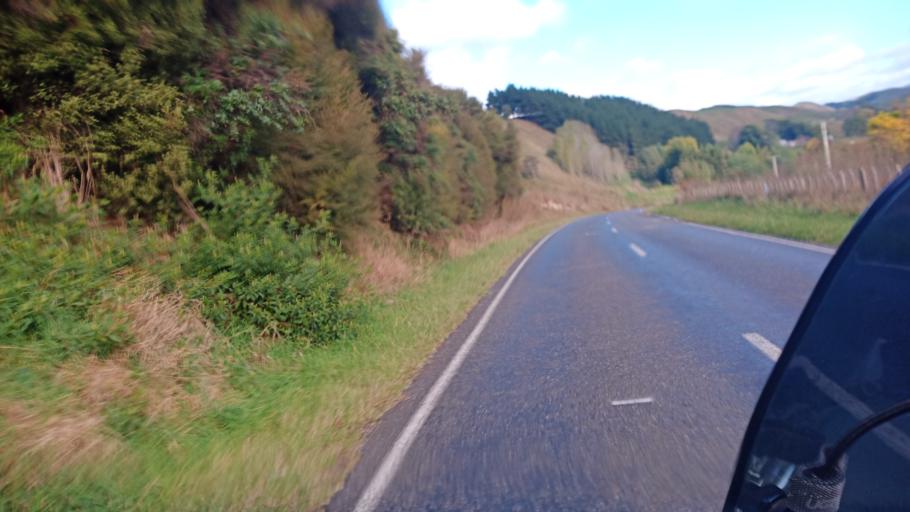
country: NZ
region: Gisborne
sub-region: Gisborne District
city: Gisborne
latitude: -38.5400
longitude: 177.5905
